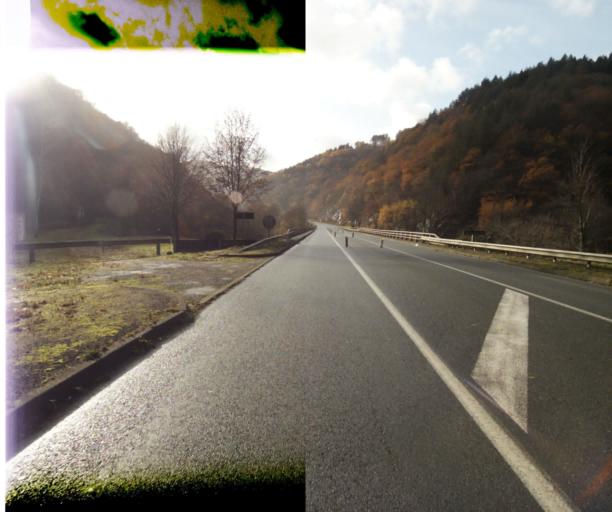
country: FR
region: Limousin
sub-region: Departement de la Correze
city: Cornil
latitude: 45.2134
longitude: 1.6888
